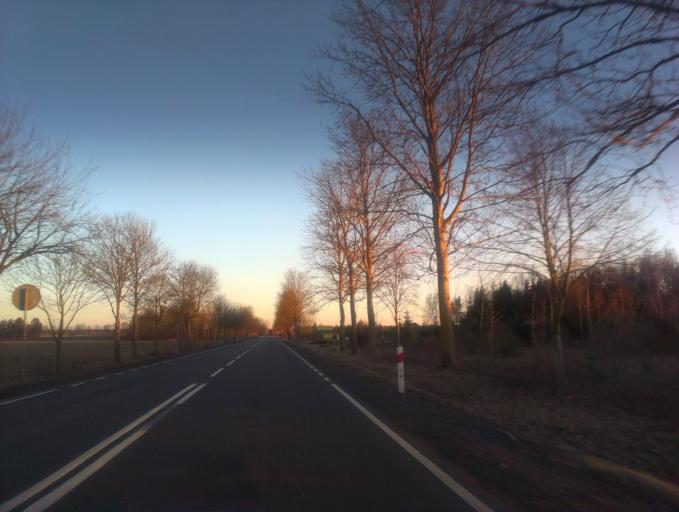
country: PL
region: West Pomeranian Voivodeship
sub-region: Powiat szczecinecki
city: Szczecinek
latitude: 53.6514
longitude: 16.7453
